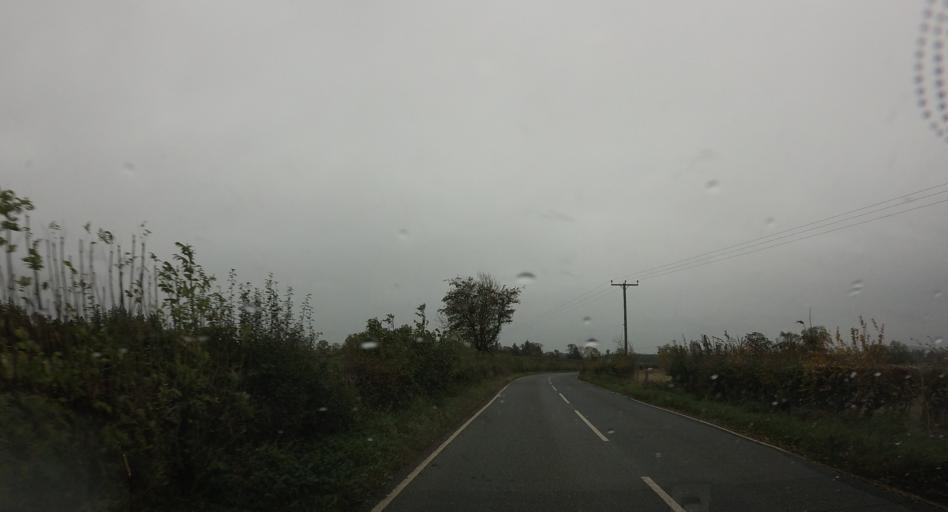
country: GB
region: Scotland
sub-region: Perth and Kinross
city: Blairgowrie
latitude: 56.5553
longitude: -3.4062
